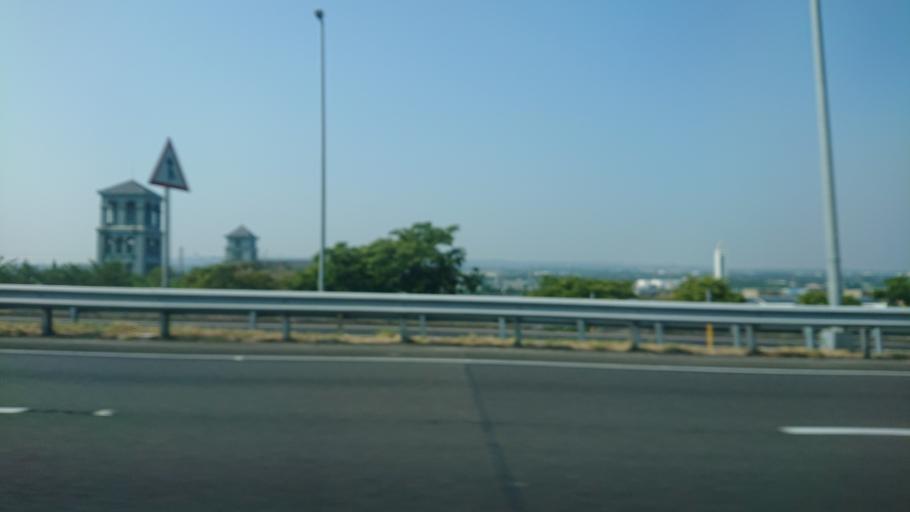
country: TW
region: Taiwan
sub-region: Nantou
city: Nantou
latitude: 23.8492
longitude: 120.7035
